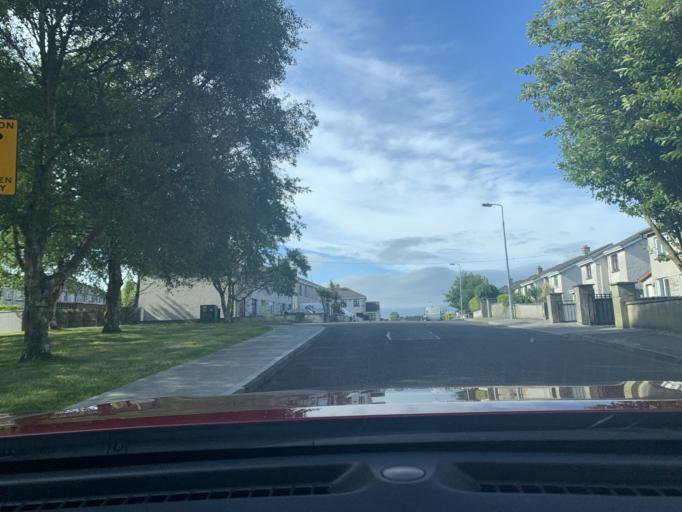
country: IE
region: Connaught
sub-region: Sligo
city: Sligo
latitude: 54.2653
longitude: -8.4992
